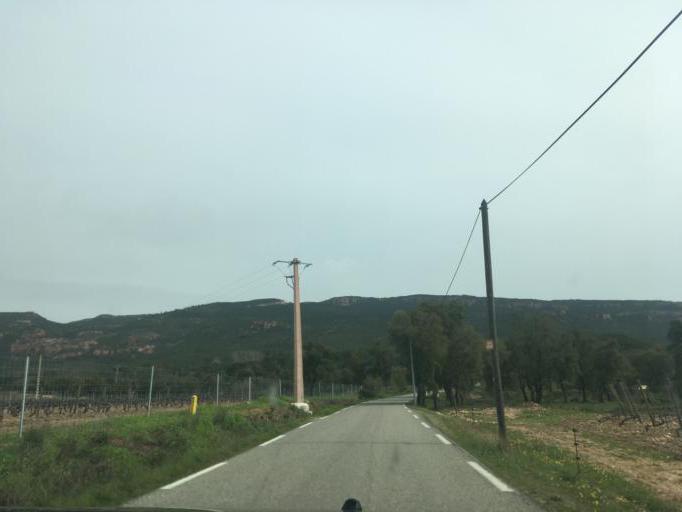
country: FR
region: Provence-Alpes-Cote d'Azur
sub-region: Departement du Var
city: Le Muy
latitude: 43.5113
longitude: 6.6137
